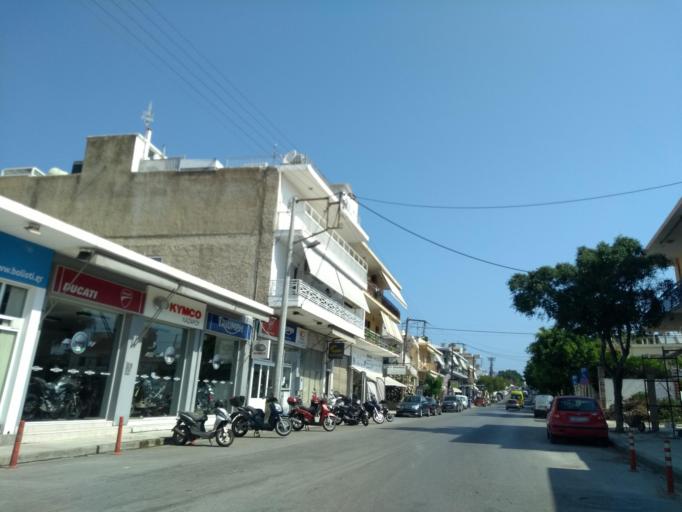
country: GR
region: Crete
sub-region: Nomos Chanias
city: Chania
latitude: 35.5042
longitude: 24.0197
